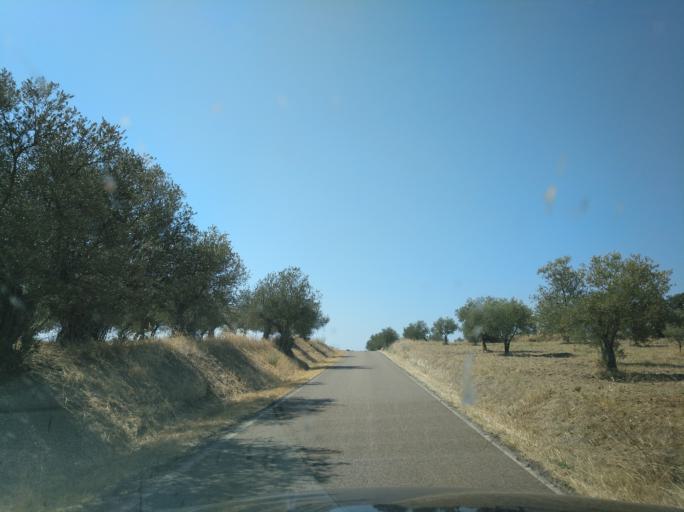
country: PT
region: Portalegre
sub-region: Campo Maior
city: Campo Maior
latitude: 39.0400
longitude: -7.0298
